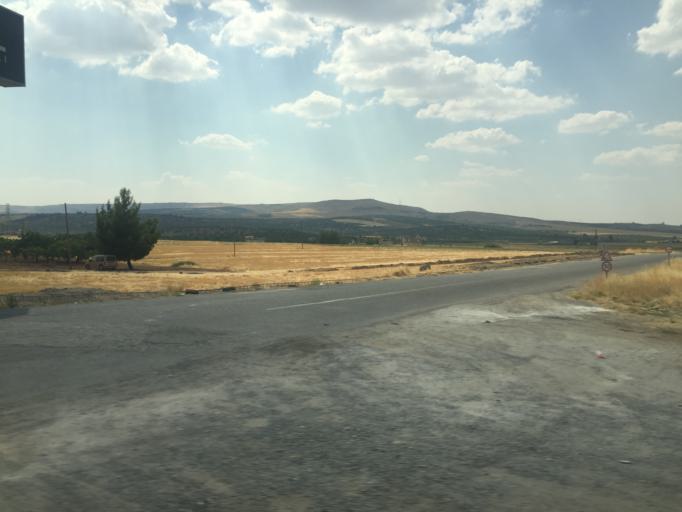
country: TR
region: Sanliurfa
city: Sanliurfa
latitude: 37.2522
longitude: 38.7929
